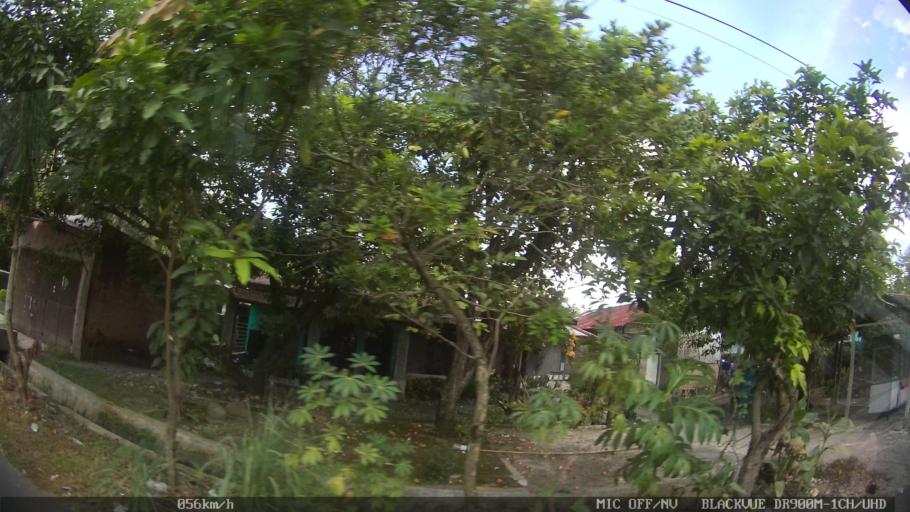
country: ID
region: North Sumatra
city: Binjai
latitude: 3.6335
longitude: 98.5027
